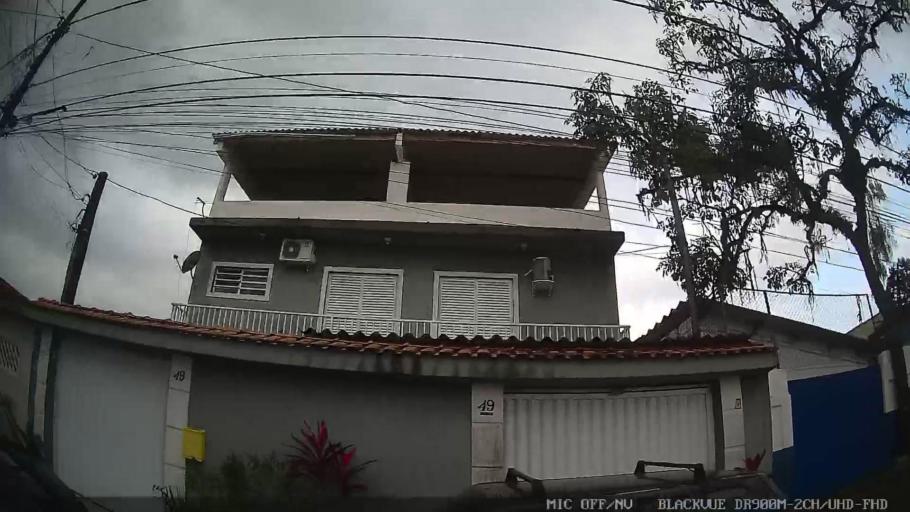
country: BR
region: Sao Paulo
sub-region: Santos
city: Santos
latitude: -23.9436
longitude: -46.2897
